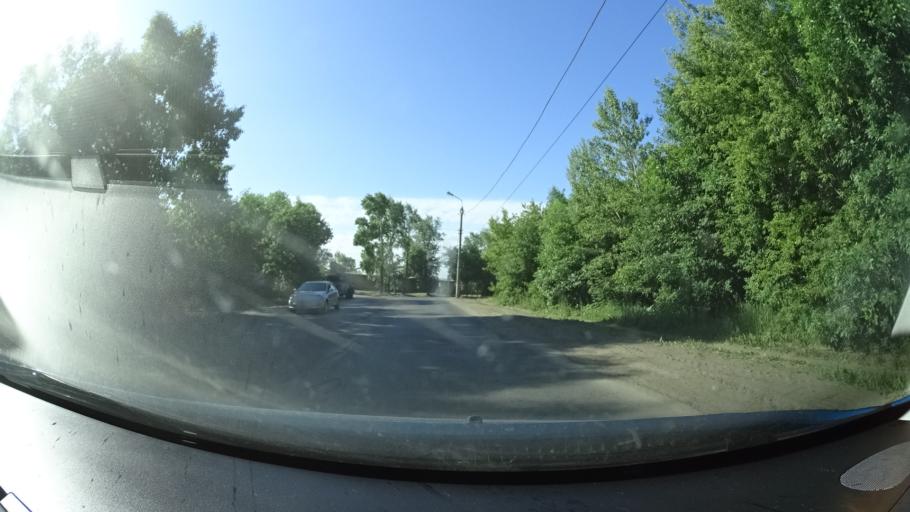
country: RU
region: Bashkortostan
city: Ufa
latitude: 54.8367
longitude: 56.0762
